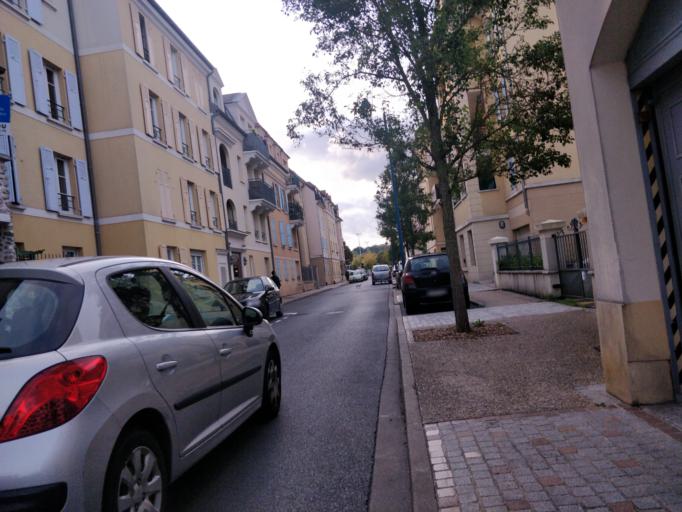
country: FR
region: Ile-de-France
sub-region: Departement du Val-d'Oise
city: Vaureal
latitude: 49.0305
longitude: 2.0203
